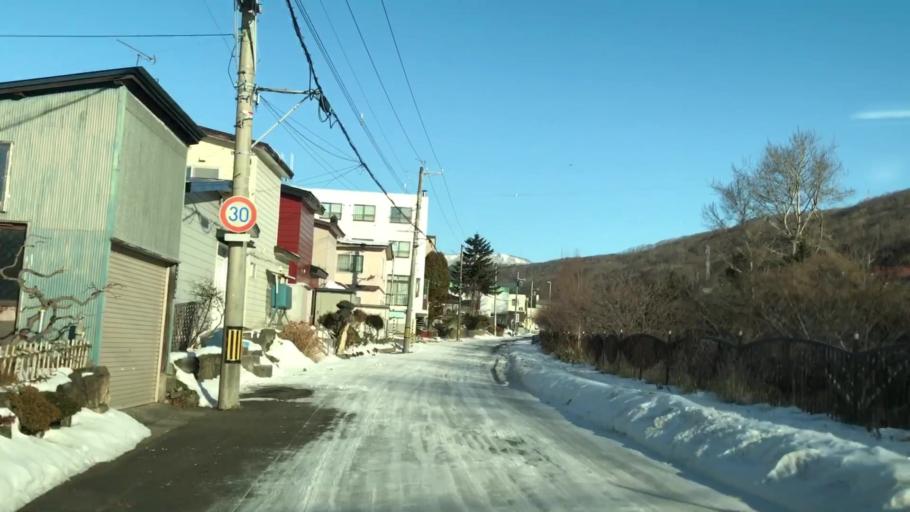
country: JP
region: Hokkaido
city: Muroran
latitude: 42.3747
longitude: 141.0375
